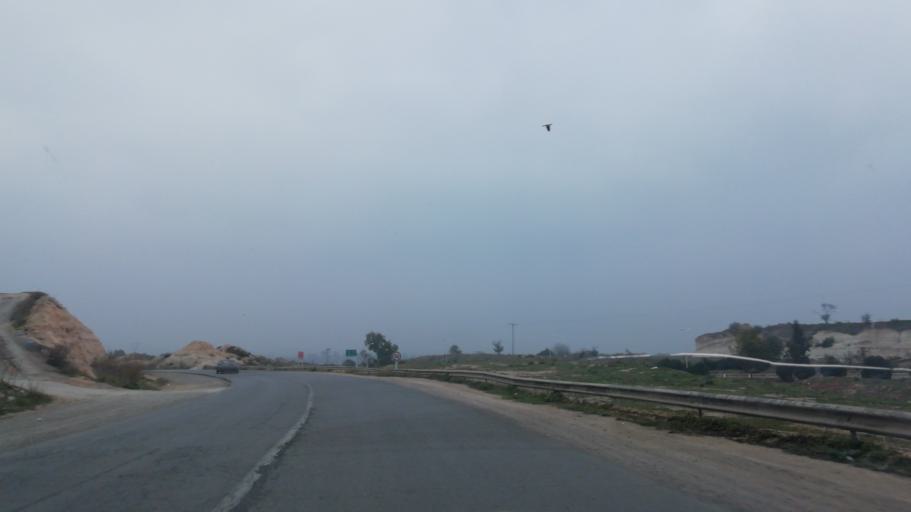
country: DZ
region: Mascara
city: Mascara
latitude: 35.3848
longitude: 0.1611
